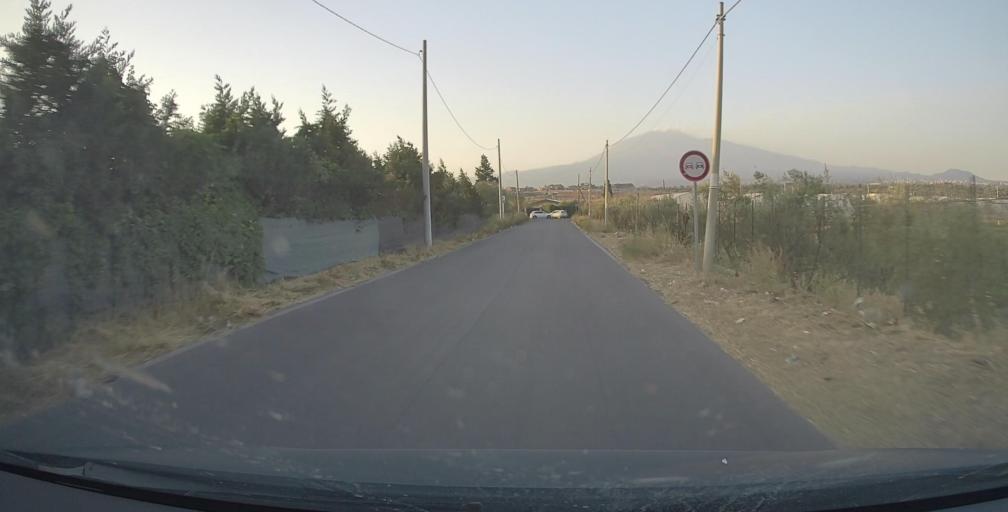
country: IT
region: Sicily
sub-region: Catania
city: Palazzolo
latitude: 37.5452
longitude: 14.9303
